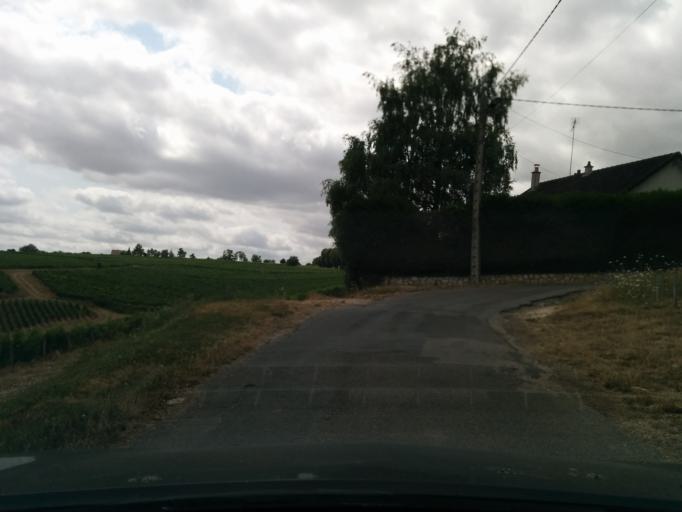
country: FR
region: Centre
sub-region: Departement du Cher
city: Sancerre
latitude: 47.3255
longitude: 2.8275
